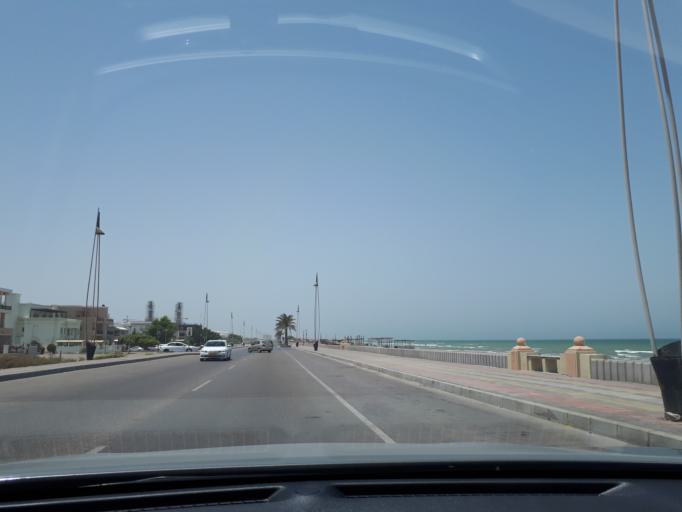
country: OM
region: Muhafazat Masqat
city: As Sib al Jadidah
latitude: 23.6428
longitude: 58.2437
